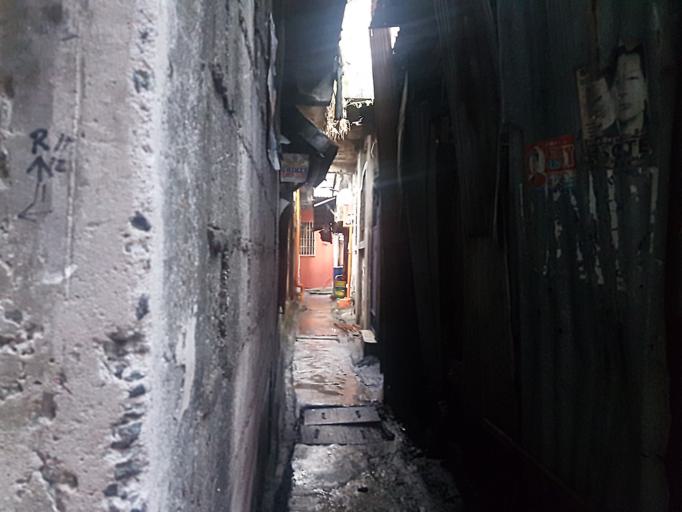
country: PH
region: Metro Manila
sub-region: City of Manila
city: Quiapo
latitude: 14.5872
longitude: 121.0004
